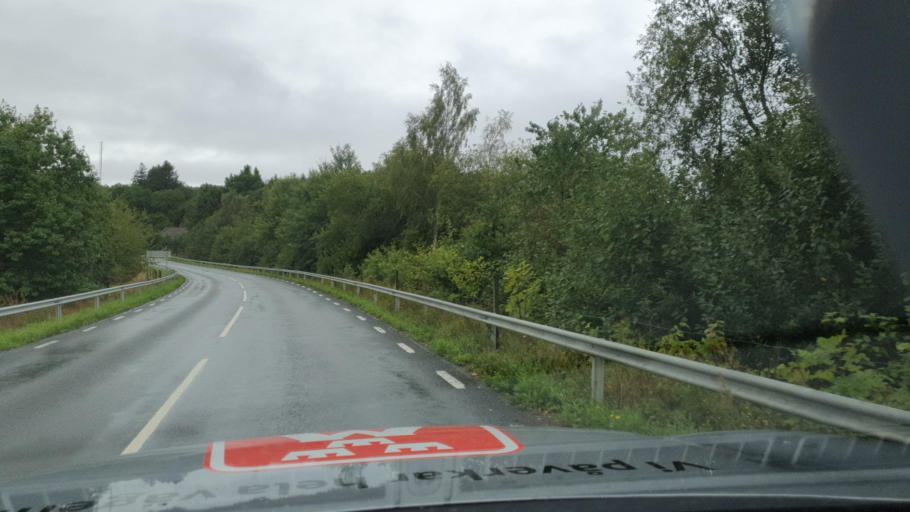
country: SE
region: Skane
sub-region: Simrishamns Kommun
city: Kivik
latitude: 55.5788
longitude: 14.1468
